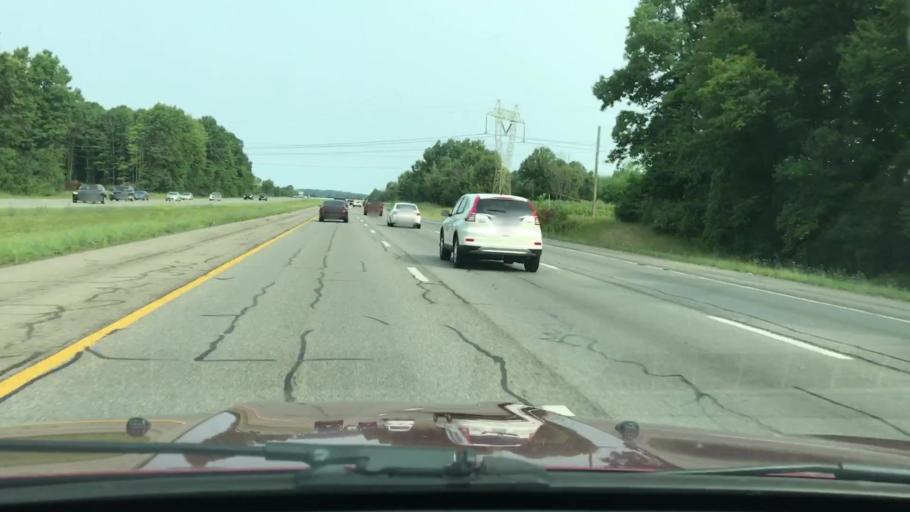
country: US
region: Ohio
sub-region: Summit County
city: Greensburg
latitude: 40.9356
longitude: -81.4384
